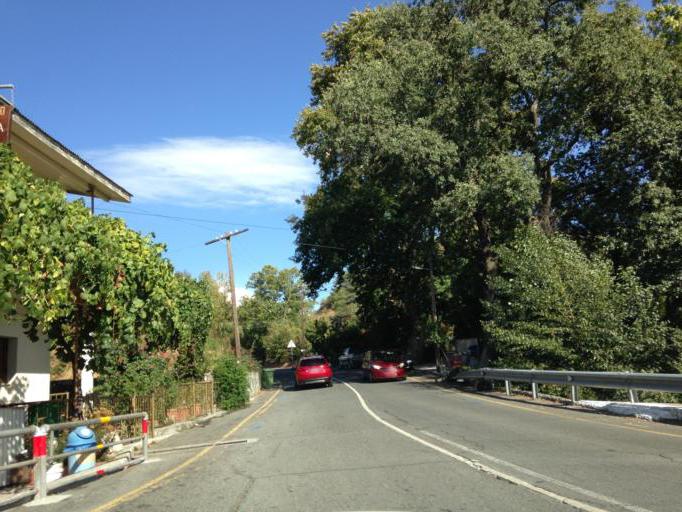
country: CY
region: Limassol
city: Pachna
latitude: 34.8799
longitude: 32.8418
